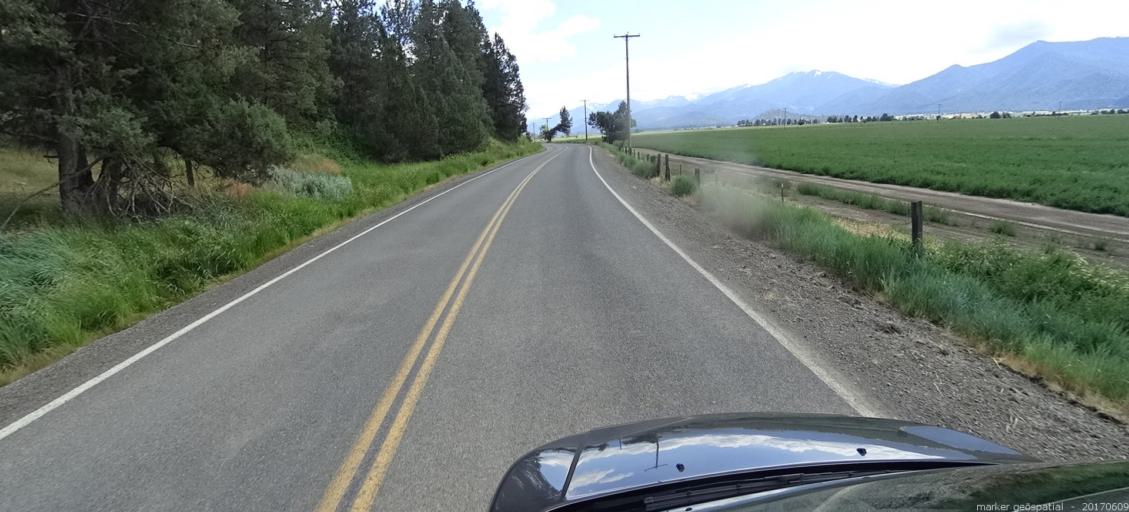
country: US
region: California
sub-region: Siskiyou County
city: Yreka
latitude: 41.5128
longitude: -122.8402
